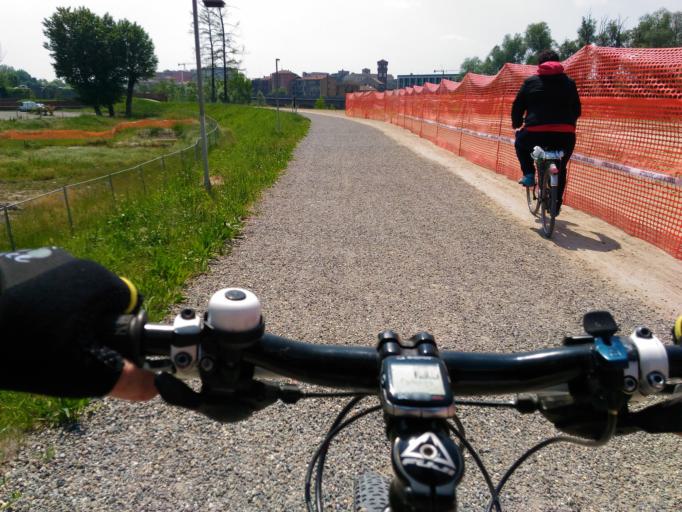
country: IT
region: Lombardy
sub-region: Provincia di Lodi
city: Lodi
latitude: 45.3214
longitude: 9.5081
